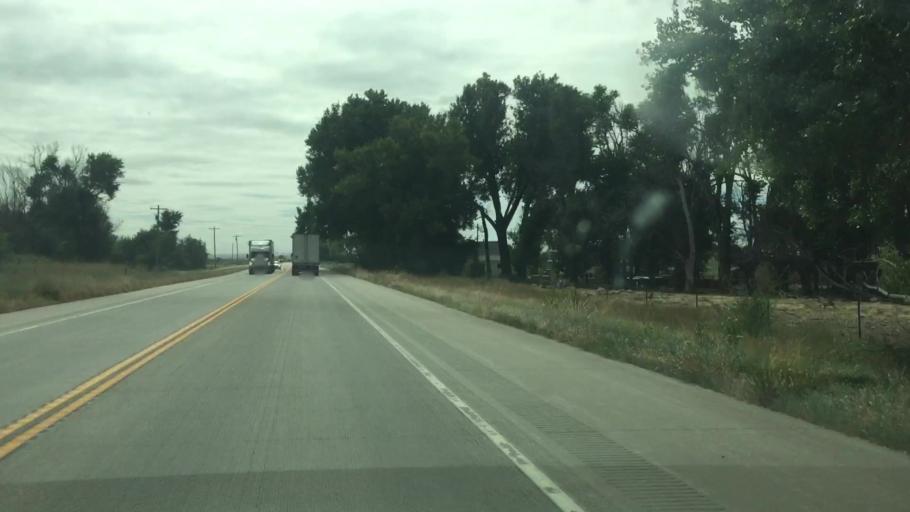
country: US
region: Colorado
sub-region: Prowers County
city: Lamar
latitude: 38.2057
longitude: -102.7242
